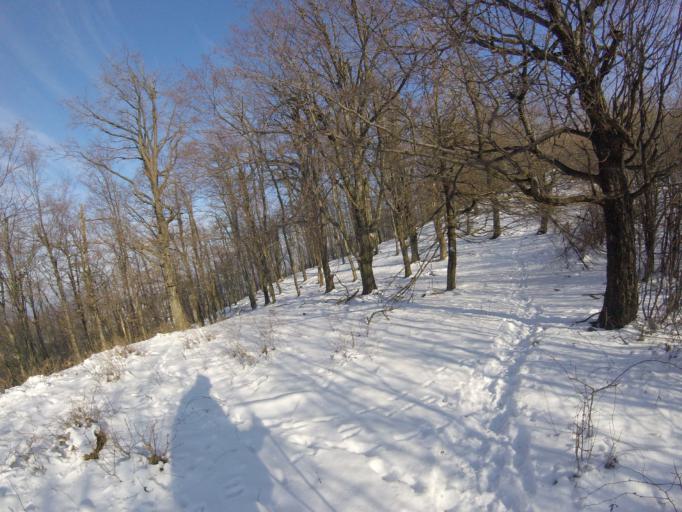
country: HU
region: Heves
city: Parad
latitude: 47.8699
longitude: 20.0601
